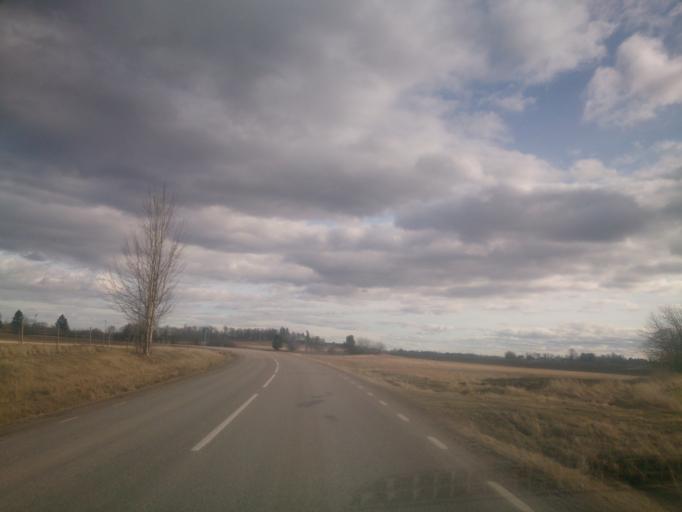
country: SE
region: OEstergoetland
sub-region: Motala Kommun
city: Borensberg
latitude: 58.4812
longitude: 15.2167
